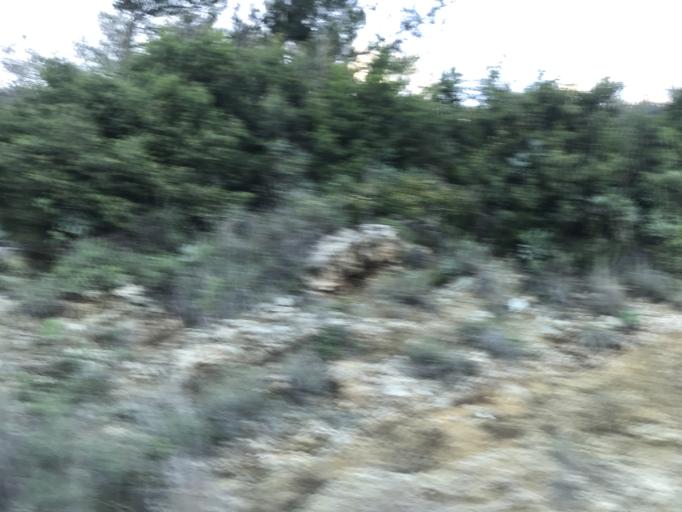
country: TR
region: Hatay
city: Buyukcat
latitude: 36.1090
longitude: 36.0484
